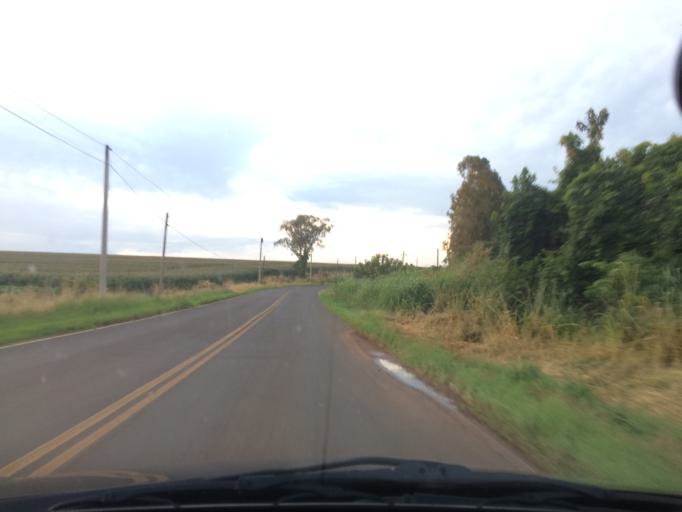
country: BR
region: Sao Paulo
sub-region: Casa Branca
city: Casa Branca
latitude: -21.7503
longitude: -47.1664
